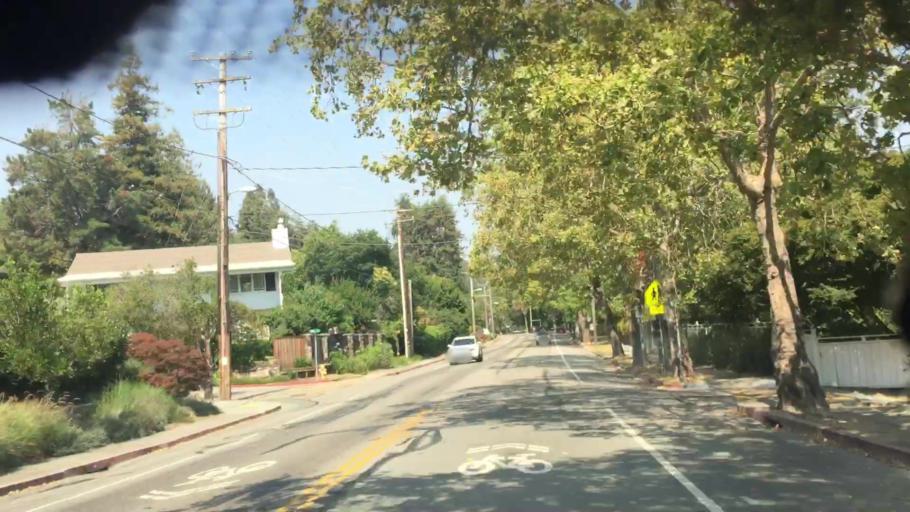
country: US
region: California
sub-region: Marin County
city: Corte Madera
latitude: 37.9277
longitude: -122.5319
